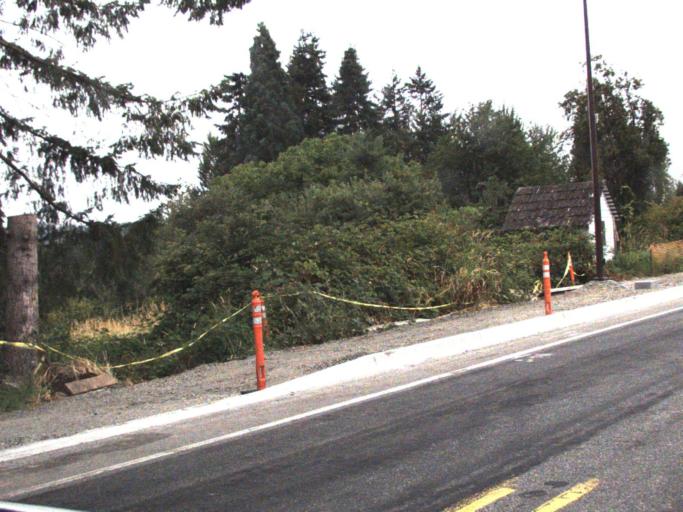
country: US
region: Washington
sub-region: King County
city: Duvall
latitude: 47.7355
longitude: -121.9874
